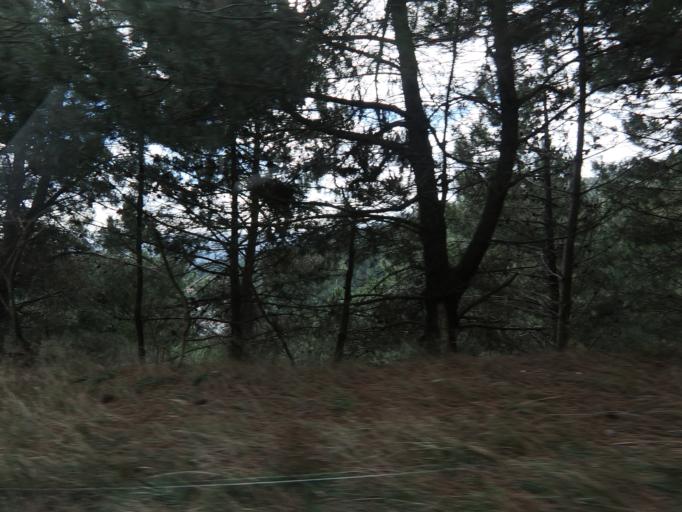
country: PT
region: Vila Real
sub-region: Vila Real
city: Vila Real
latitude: 41.3343
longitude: -7.7736
